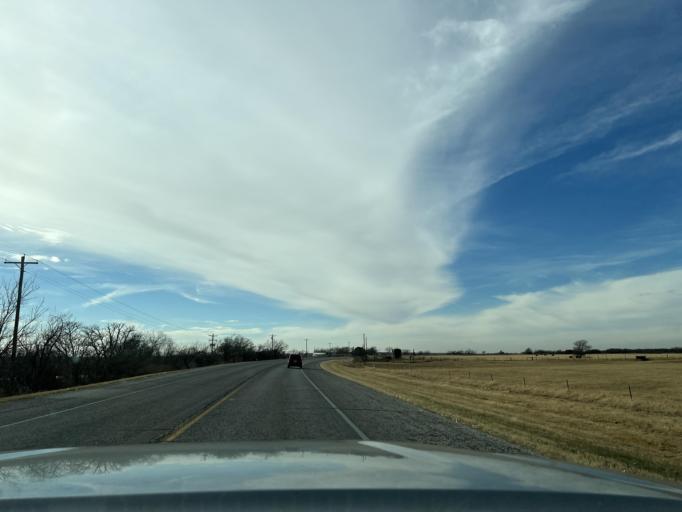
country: US
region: Texas
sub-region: Fisher County
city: Roby
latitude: 32.7541
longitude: -100.2608
